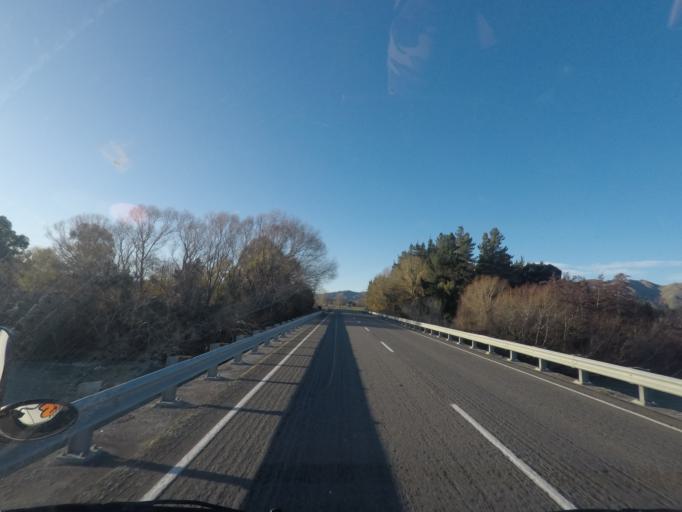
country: NZ
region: Canterbury
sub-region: Kaikoura District
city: Kaikoura
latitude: -42.7201
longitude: 173.2854
